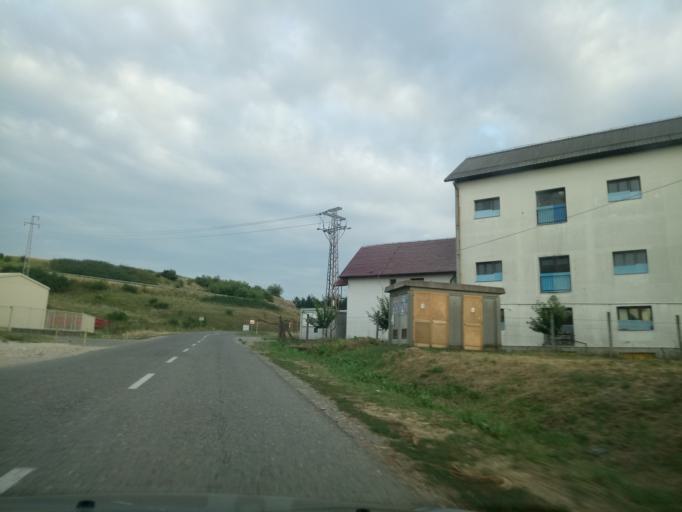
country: RS
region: Autonomna Pokrajina Vojvodina
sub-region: Sremski Okrug
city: Irig
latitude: 45.0947
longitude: 19.8653
